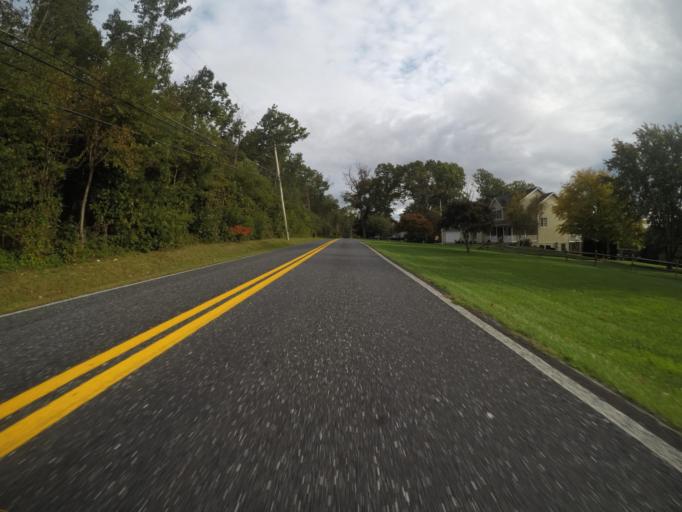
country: US
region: Maryland
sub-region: Carroll County
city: Hampstead
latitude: 39.5634
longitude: -76.8824
